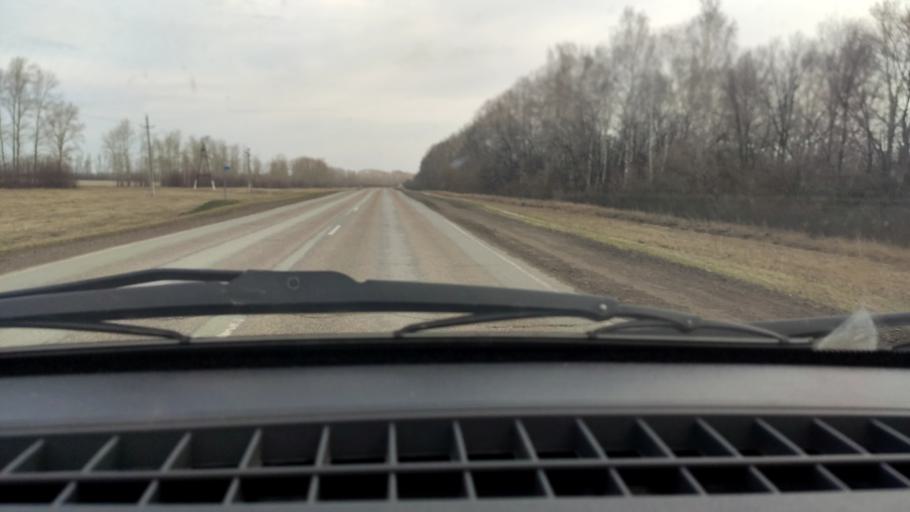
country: RU
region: Bashkortostan
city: Davlekanovo
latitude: 54.3427
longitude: 55.1737
